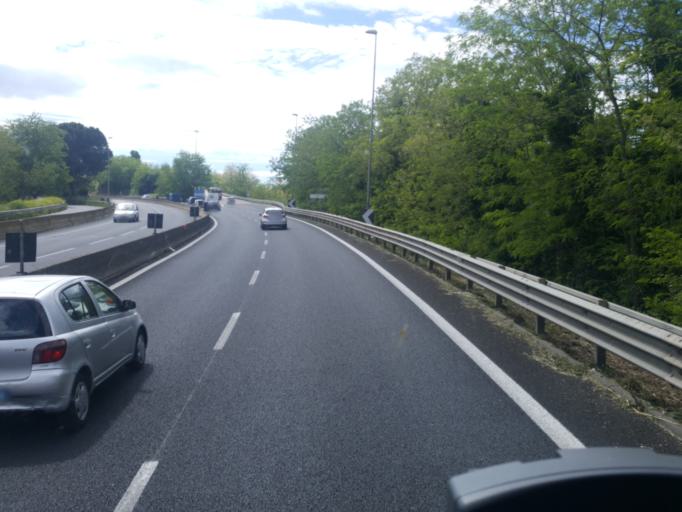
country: IT
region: Latium
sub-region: Citta metropolitana di Roma Capitale
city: La Massimina-Casal Lumbroso
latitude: 41.8883
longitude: 12.3687
